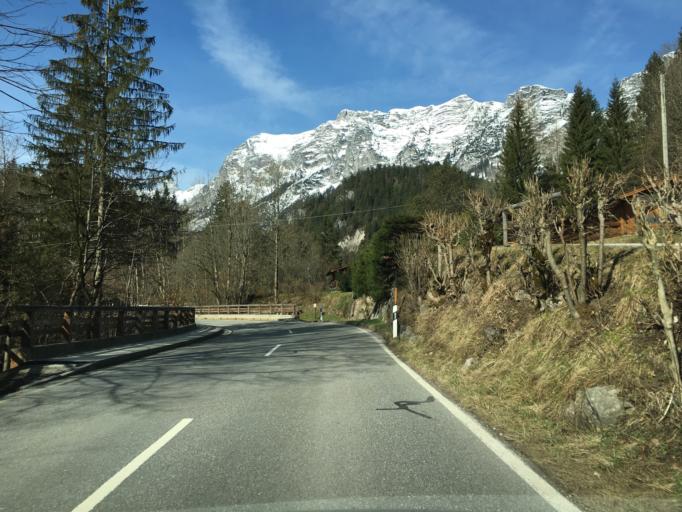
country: DE
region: Bavaria
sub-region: Upper Bavaria
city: Ramsau
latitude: 47.6093
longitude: 12.8781
